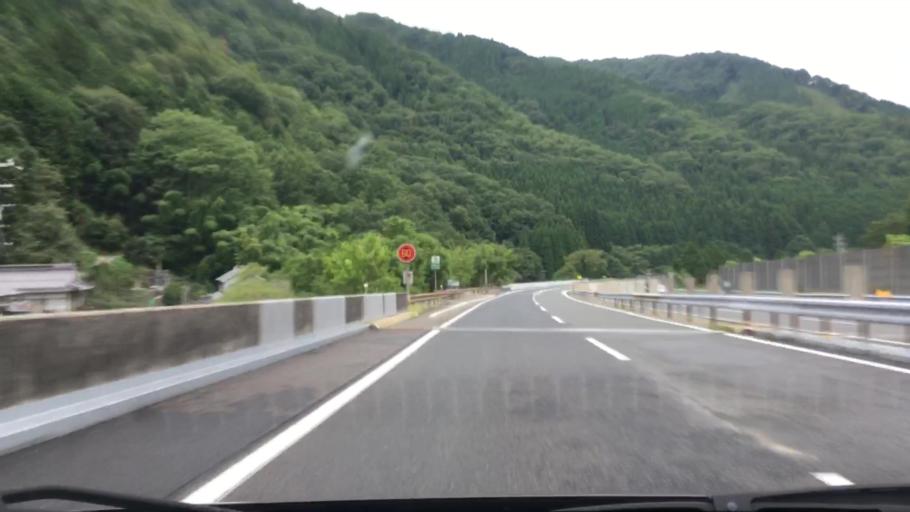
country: JP
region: Okayama
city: Niimi
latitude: 35.0083
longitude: 133.4911
